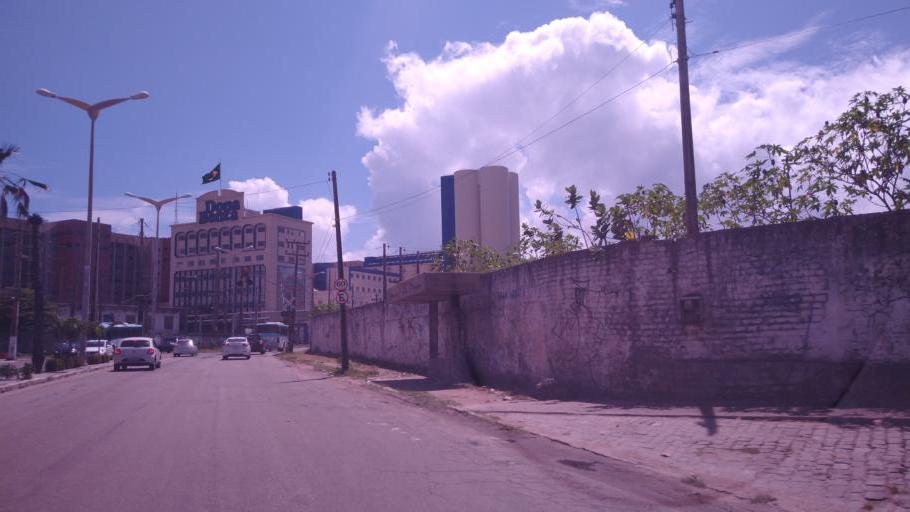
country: BR
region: Ceara
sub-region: Fortaleza
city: Fortaleza
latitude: -3.7180
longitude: -38.4751
